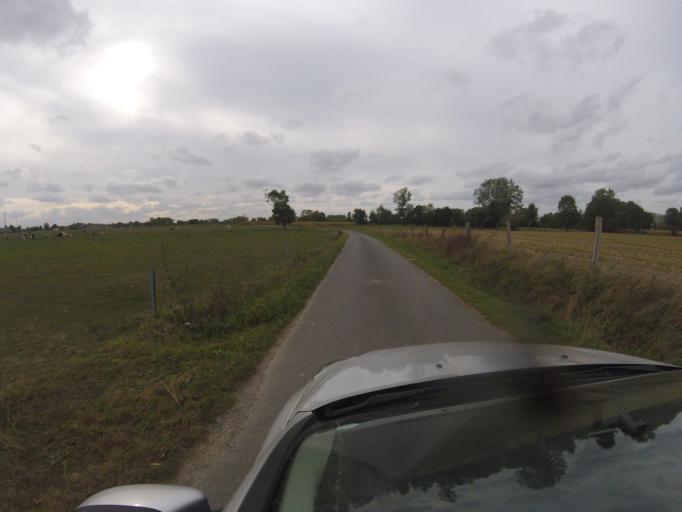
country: FR
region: Lower Normandy
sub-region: Departement de la Manche
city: Le Val-Saint-Pere
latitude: 48.6380
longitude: -1.3925
